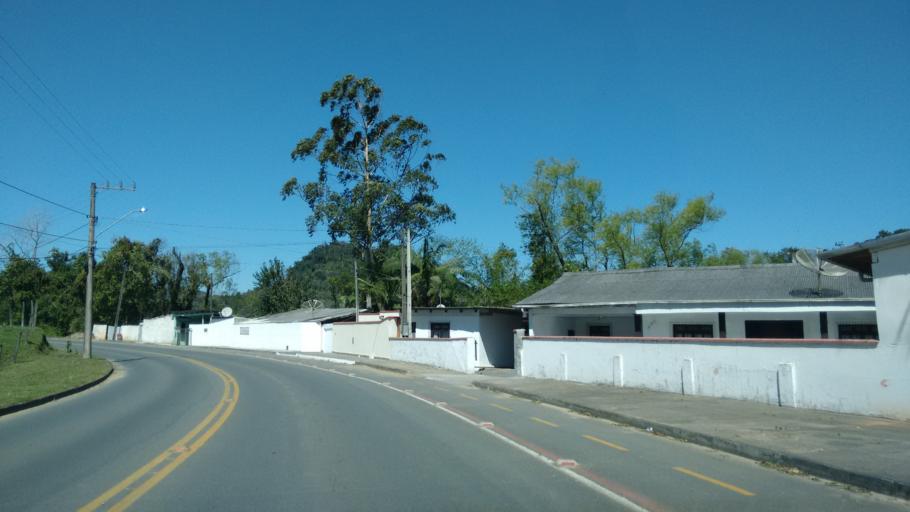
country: BR
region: Santa Catarina
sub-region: Blumenau
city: Blumenau
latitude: -26.8877
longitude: -49.1346
